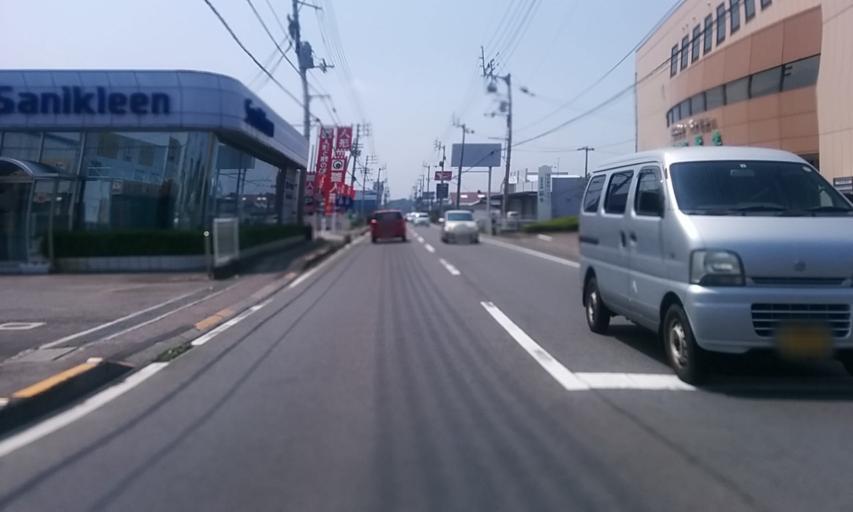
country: JP
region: Ehime
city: Niihama
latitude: 33.9302
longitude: 133.2767
